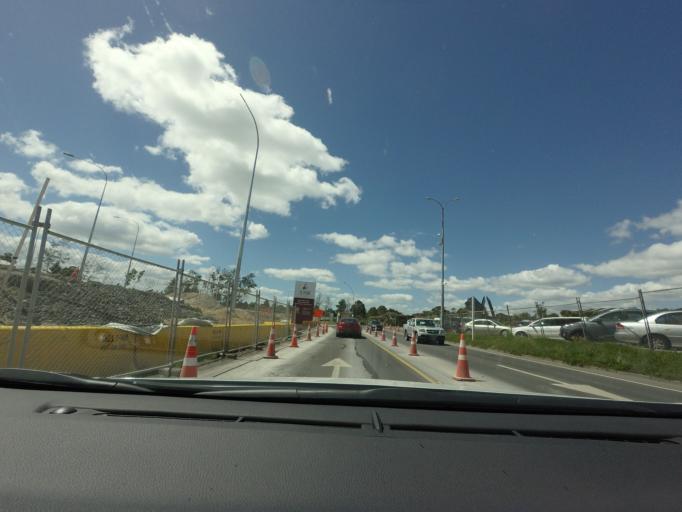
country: NZ
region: Bay of Plenty
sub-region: Rotorua District
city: Rotorua
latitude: -38.1653
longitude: 176.2472
